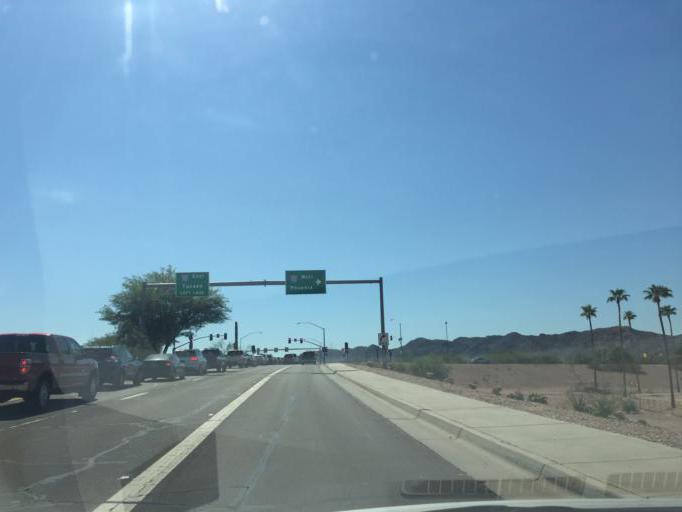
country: US
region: Arizona
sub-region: Maricopa County
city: Guadalupe
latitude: 33.3345
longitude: -111.9696
